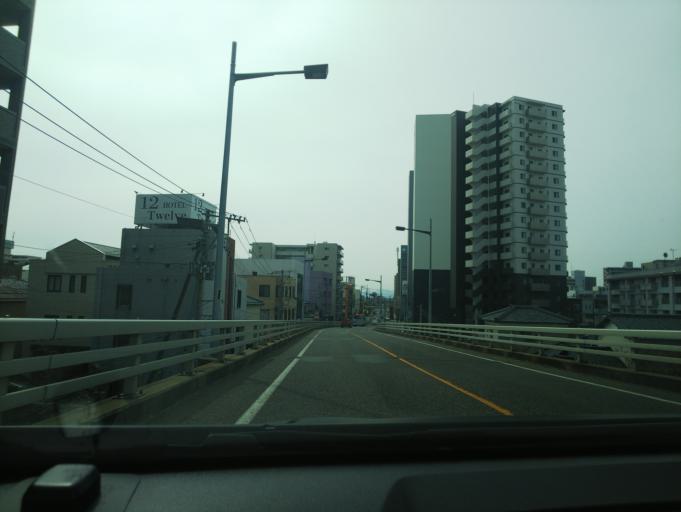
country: JP
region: Niigata
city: Niigata-shi
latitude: 37.9129
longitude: 139.0672
